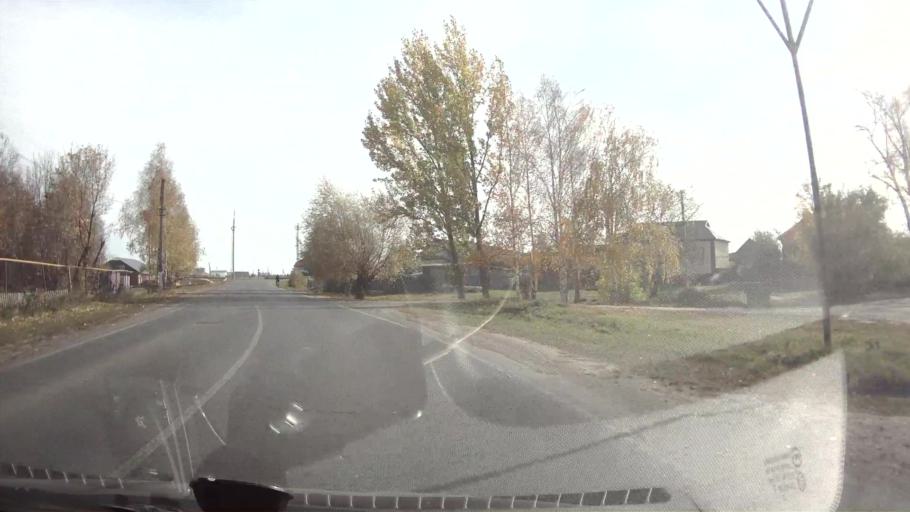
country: RU
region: Mordoviya
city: Turgenevo
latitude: 54.8442
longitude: 46.3494
